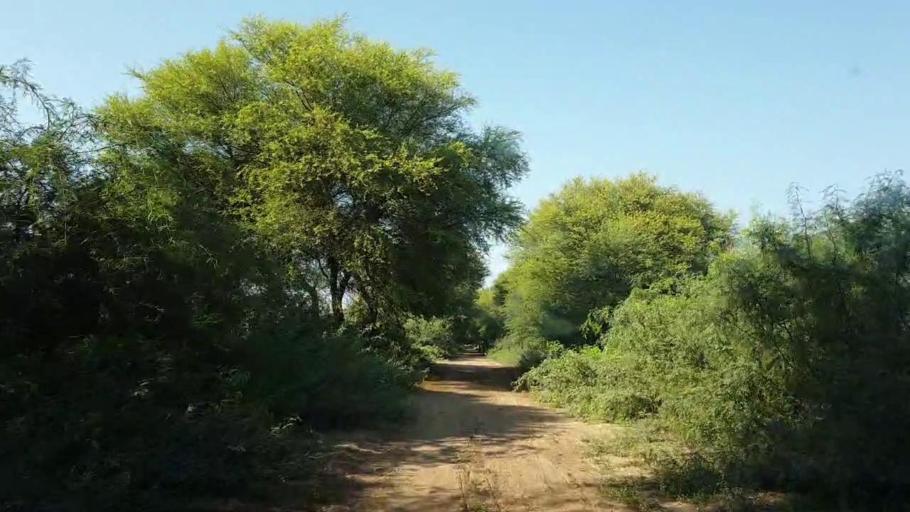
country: PK
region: Sindh
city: Tando Jam
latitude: 25.3547
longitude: 68.5699
